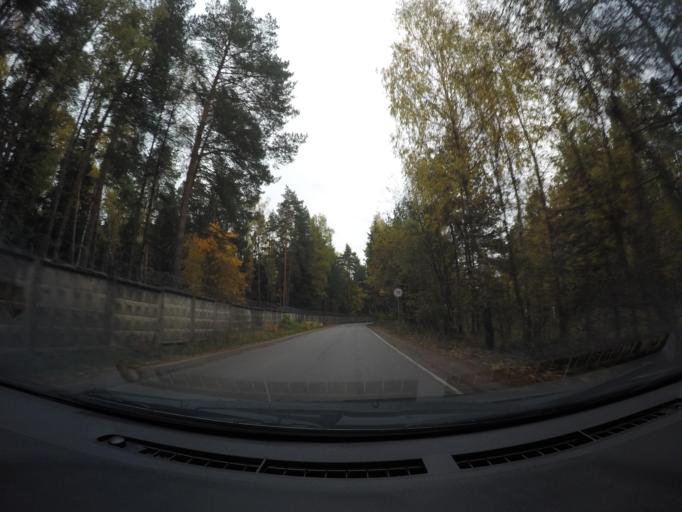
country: RU
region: Moskovskaya
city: Vishnyakovskiye Dachi
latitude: 55.8079
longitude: 38.1114
